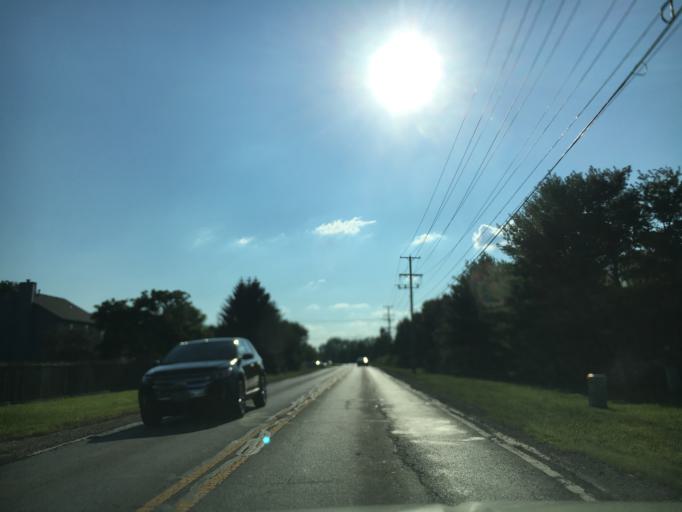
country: US
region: Ohio
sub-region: Franklin County
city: Hilliard
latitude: 40.0043
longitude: -83.1644
